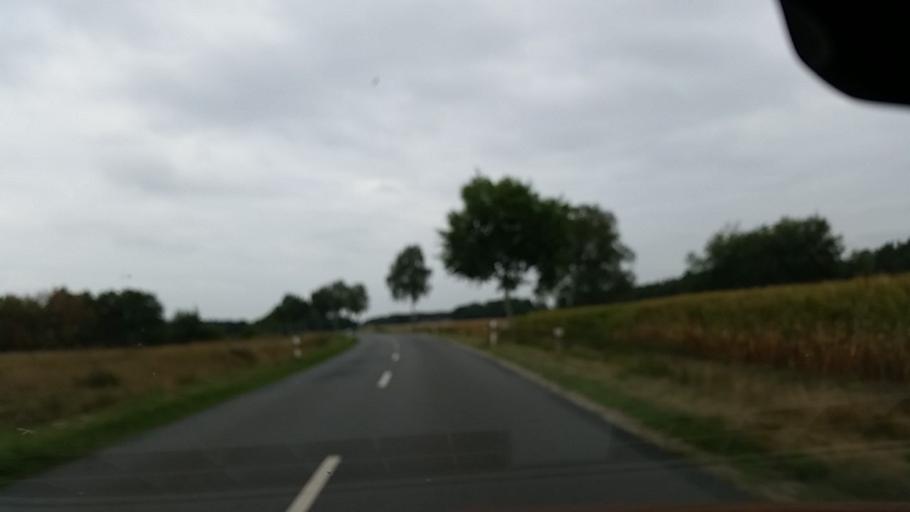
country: DE
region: Lower Saxony
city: Schoneworde
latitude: 52.5916
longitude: 10.6812
